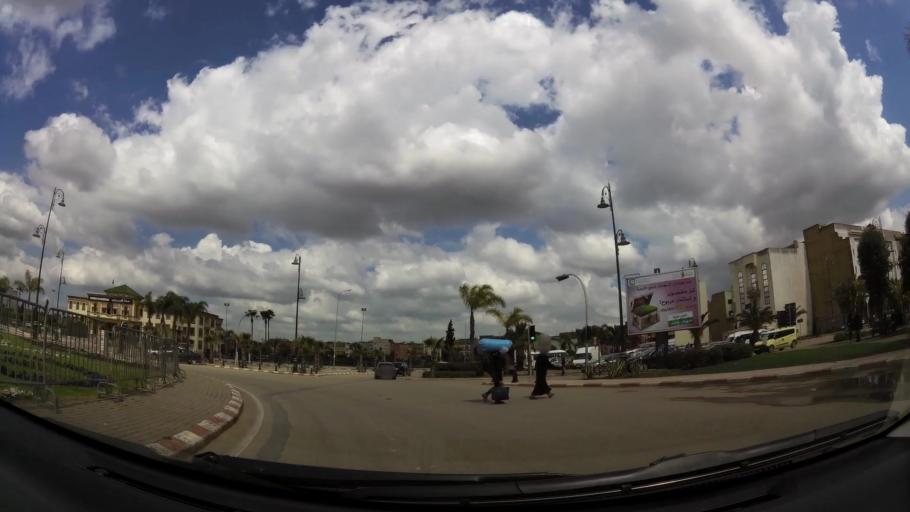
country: MA
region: Chaouia-Ouardigha
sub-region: Settat Province
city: Berrechid
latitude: 33.2651
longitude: -7.5832
